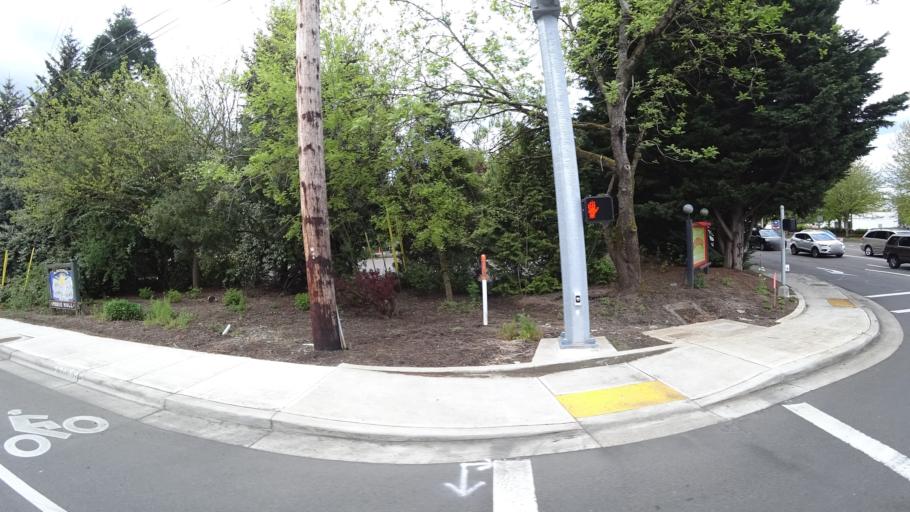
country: US
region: Oregon
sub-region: Washington County
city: Rockcreek
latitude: 45.5500
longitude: -122.9001
